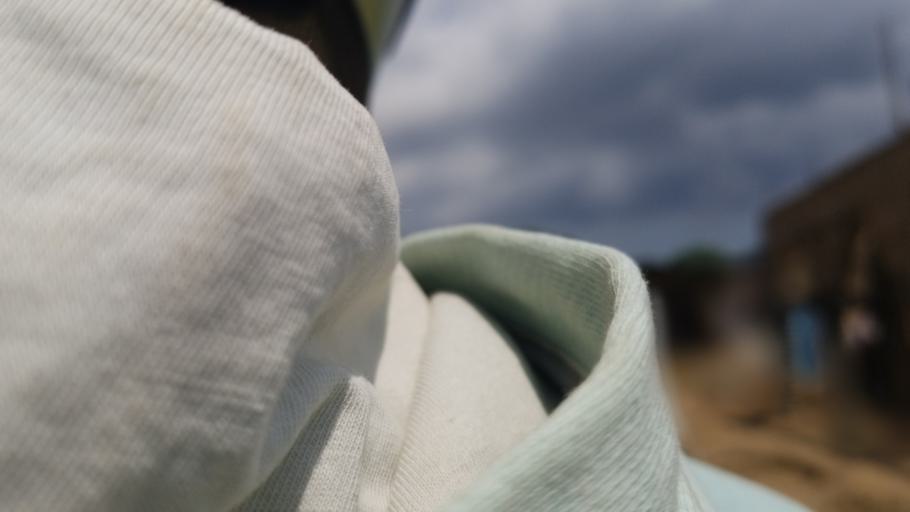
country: SL
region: Western Area
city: Waterloo
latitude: 8.3204
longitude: -13.0506
